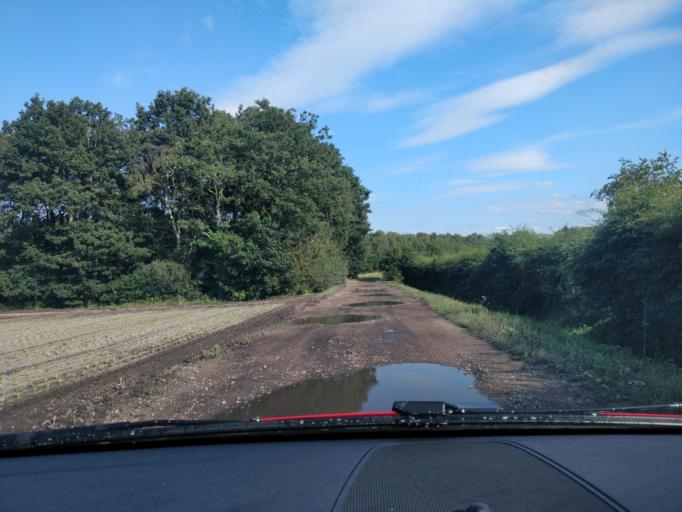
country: GB
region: England
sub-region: Lancashire
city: Banks
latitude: 53.6544
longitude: -2.9012
